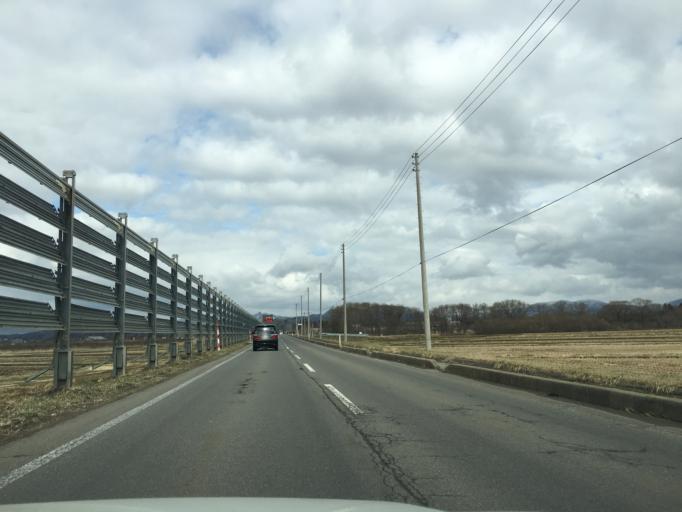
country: JP
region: Akita
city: Hanawa
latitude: 40.2511
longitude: 140.7582
